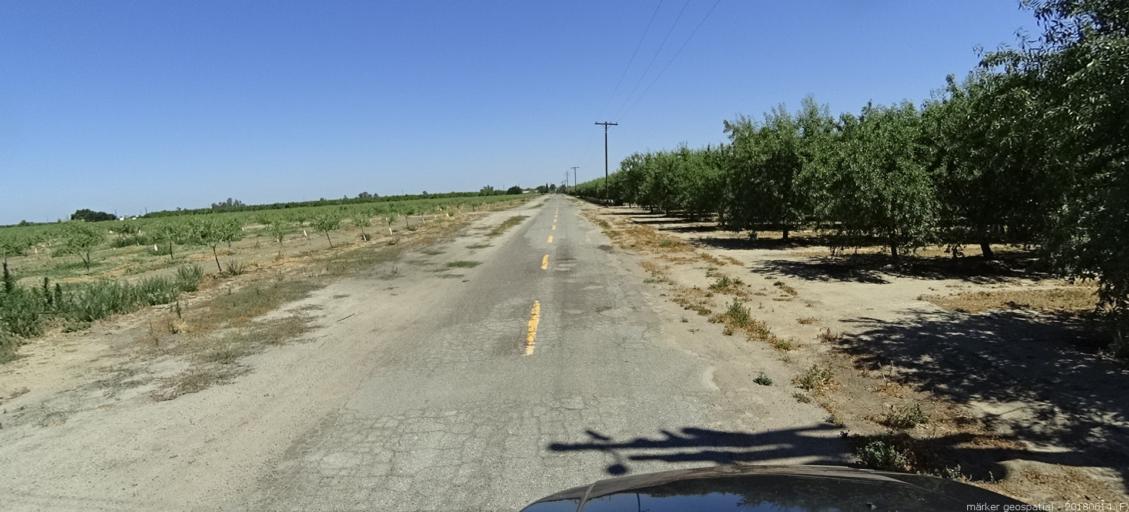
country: US
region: California
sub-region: Madera County
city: Fairmead
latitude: 36.9922
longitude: -120.2476
